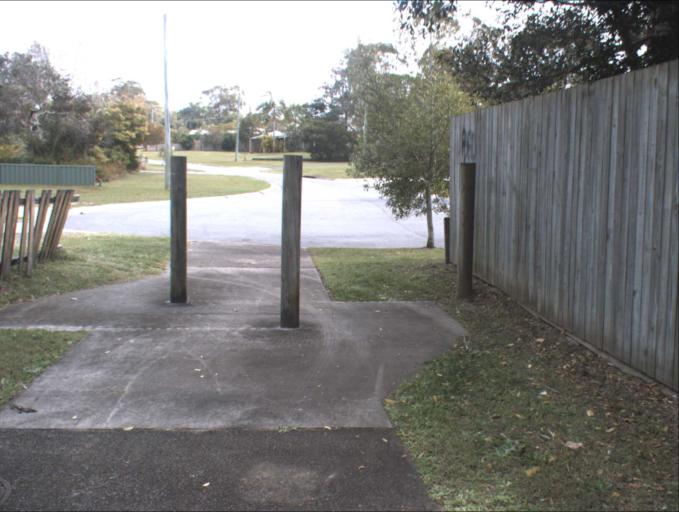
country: AU
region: Queensland
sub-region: Logan
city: Logan Reserve
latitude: -27.6819
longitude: 153.0664
